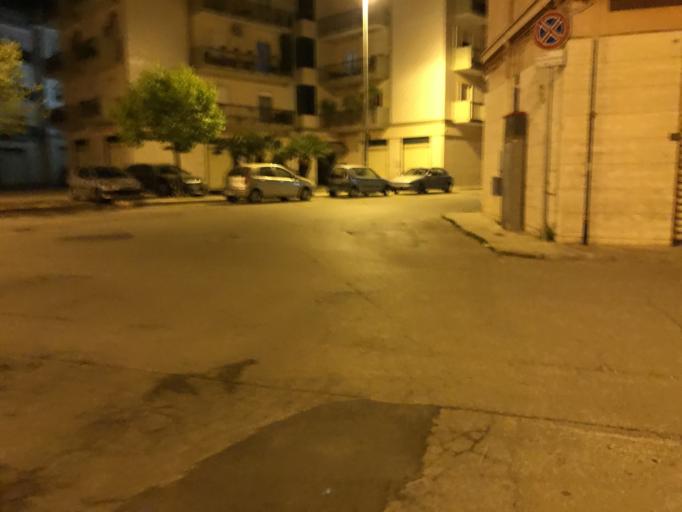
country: IT
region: Apulia
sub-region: Provincia di Bari
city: Corato
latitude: 41.1512
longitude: 16.4039
